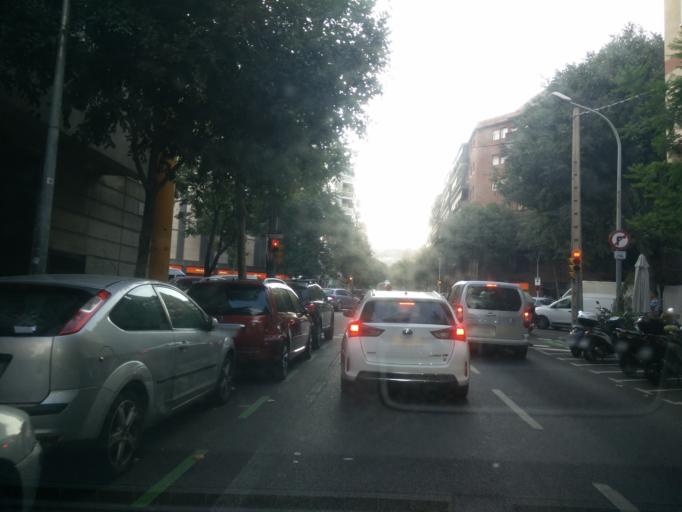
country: ES
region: Catalonia
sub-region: Provincia de Barcelona
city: Horta-Guinardo
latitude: 41.4074
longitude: 2.1792
